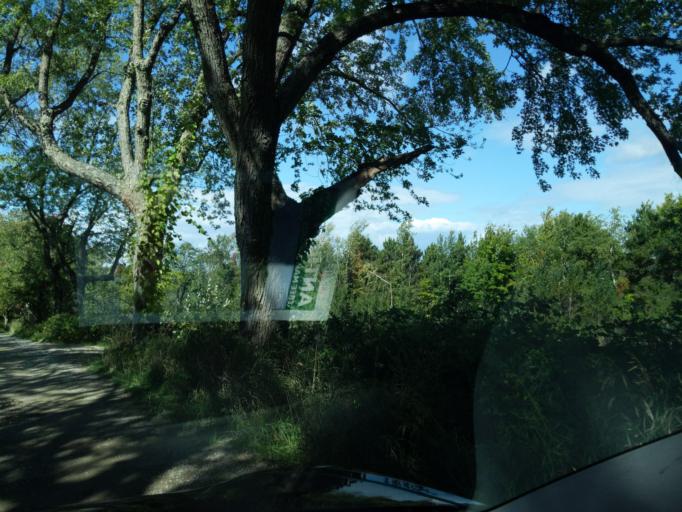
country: US
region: Michigan
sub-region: Antrim County
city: Elk Rapids
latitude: 44.9455
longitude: -85.3329
